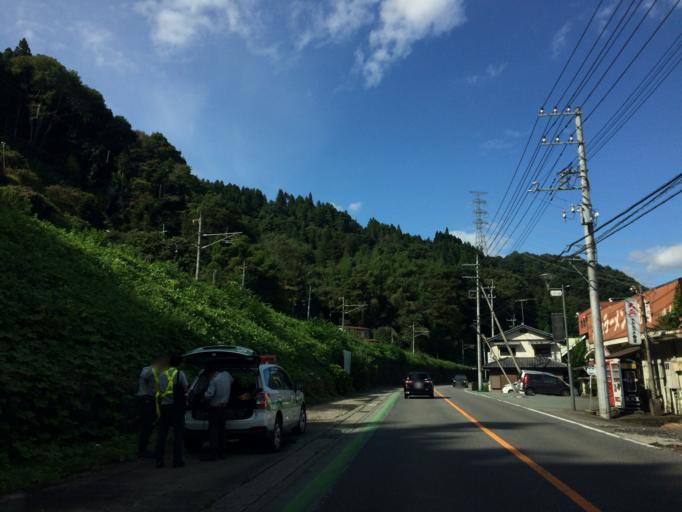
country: JP
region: Gunma
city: Nakanojomachi
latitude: 36.5581
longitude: 138.8101
